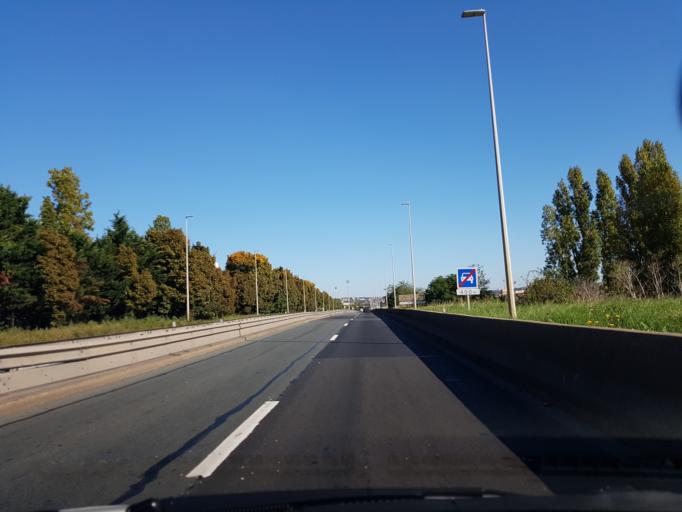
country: FR
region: Ile-de-France
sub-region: Departement du Val-de-Marne
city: Bonneuil-sur-Marne
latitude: 48.7618
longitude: 2.4724
